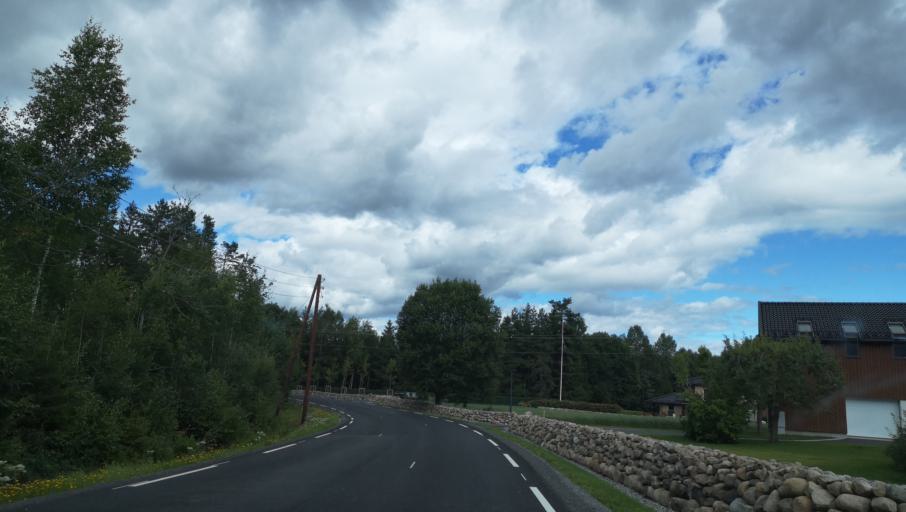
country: NO
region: Ostfold
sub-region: Hobol
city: Elvestad
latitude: 59.6868
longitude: 10.9350
